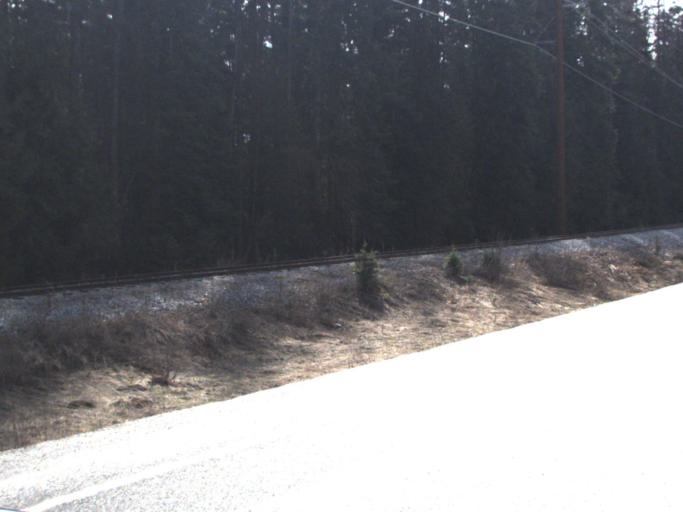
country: US
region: Washington
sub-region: Stevens County
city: Chewelah
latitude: 48.5771
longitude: -117.3522
